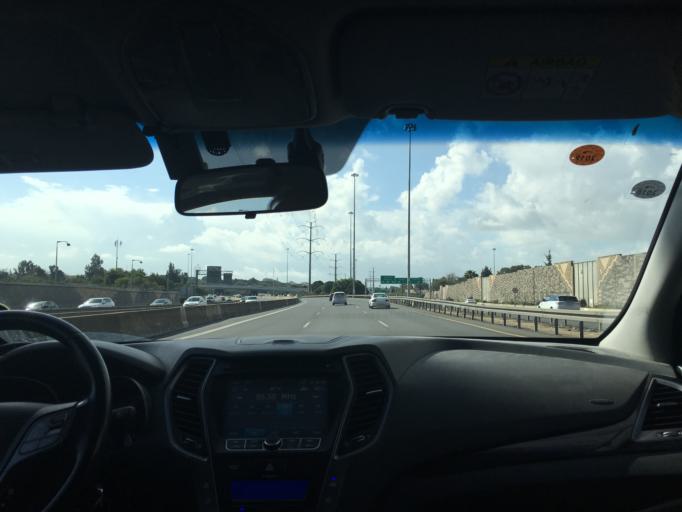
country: IL
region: Tel Aviv
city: Bene Beraq
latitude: 32.0600
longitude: 34.8357
